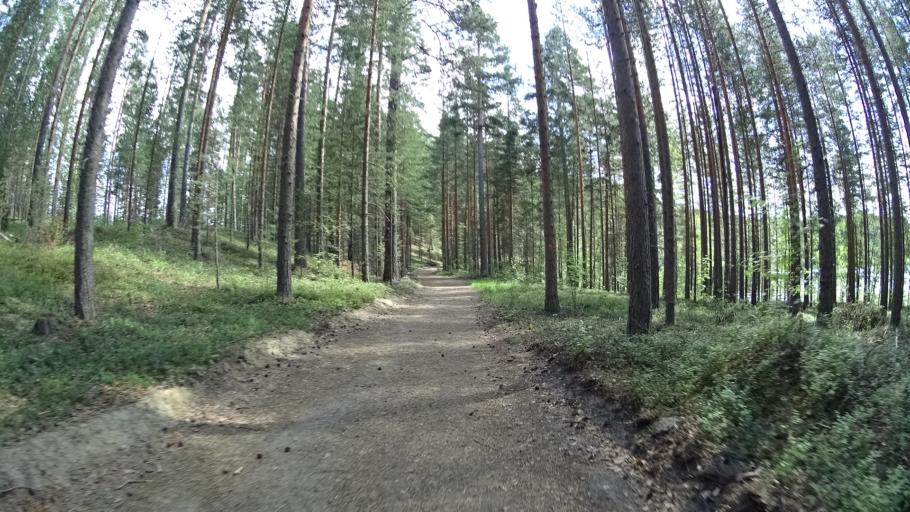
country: FI
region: Southern Savonia
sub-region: Savonlinna
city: Punkaharju
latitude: 61.7913
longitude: 29.3053
